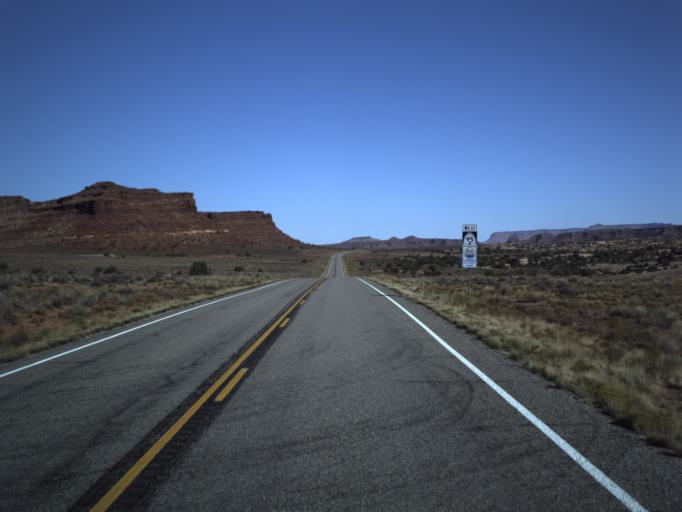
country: US
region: Utah
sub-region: San Juan County
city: Blanding
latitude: 37.7572
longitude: -110.2820
